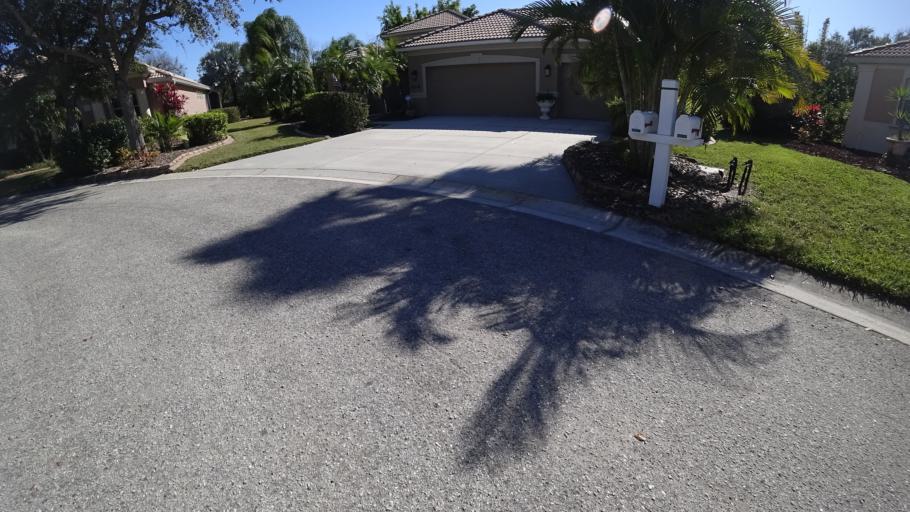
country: US
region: Florida
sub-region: Sarasota County
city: Desoto Lakes
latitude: 27.4204
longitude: -82.4643
